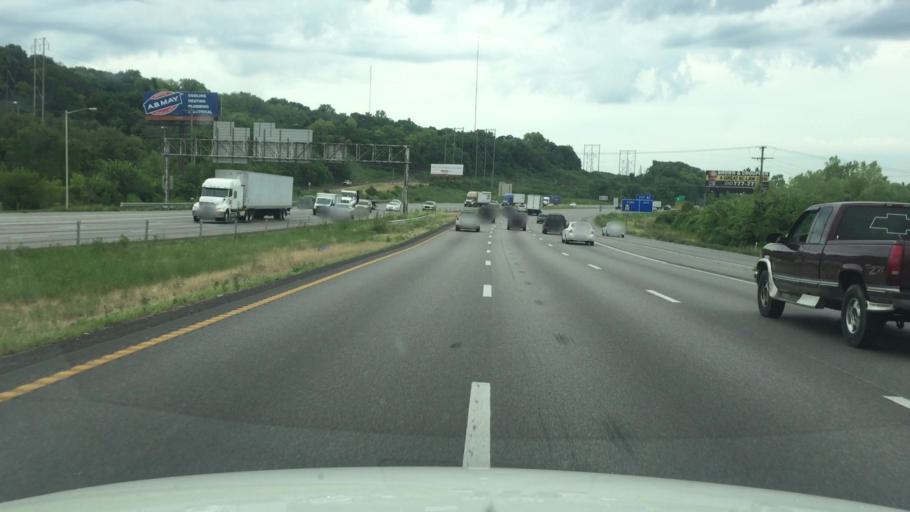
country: US
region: Missouri
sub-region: Jackson County
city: Sugar Creek
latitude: 39.0906
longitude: -94.4876
